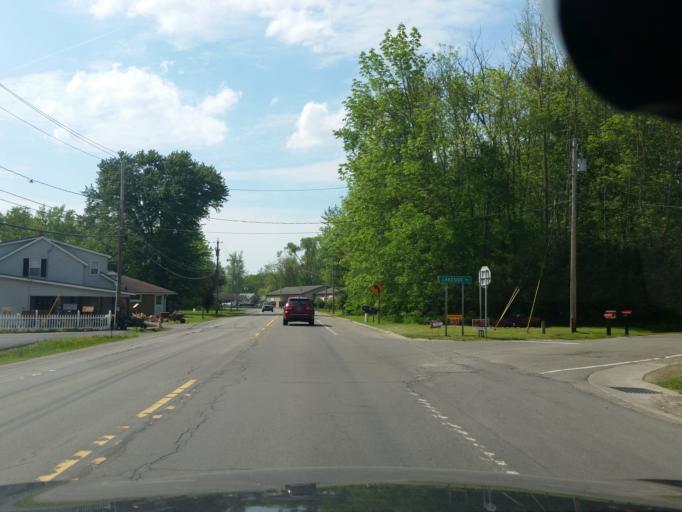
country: US
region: New York
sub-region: Chautauqua County
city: Lakewood
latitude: 42.1022
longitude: -79.3579
